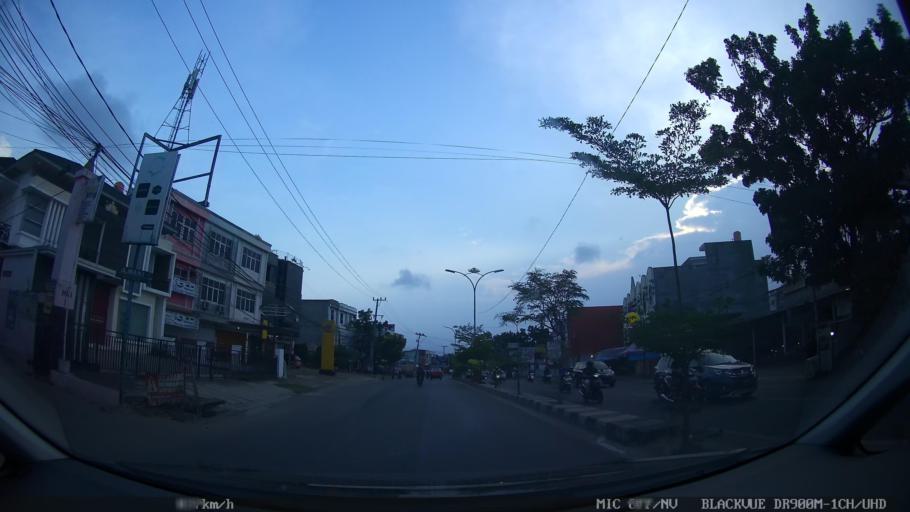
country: ID
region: Lampung
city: Kedaton
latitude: -5.3993
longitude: 105.2879
